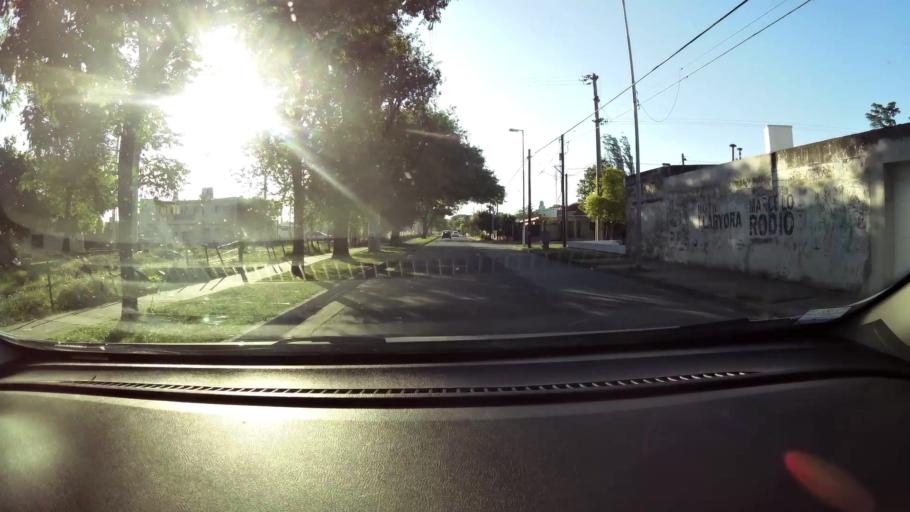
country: AR
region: Cordoba
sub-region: Departamento de Capital
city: Cordoba
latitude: -31.3713
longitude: -64.2032
